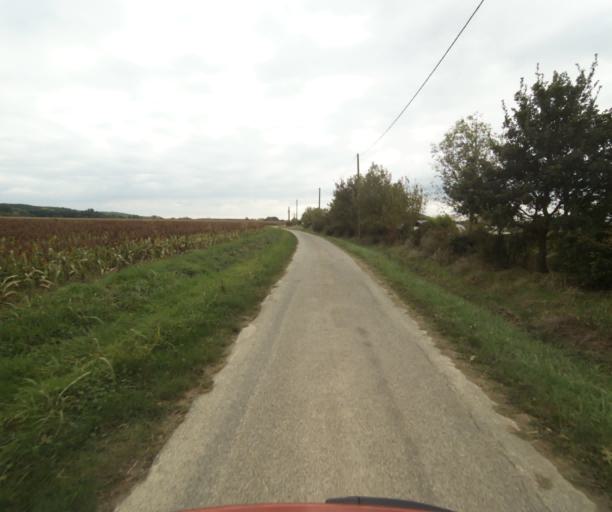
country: FR
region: Midi-Pyrenees
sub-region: Departement du Tarn-et-Garonne
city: Finhan
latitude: 43.8976
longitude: 1.2641
